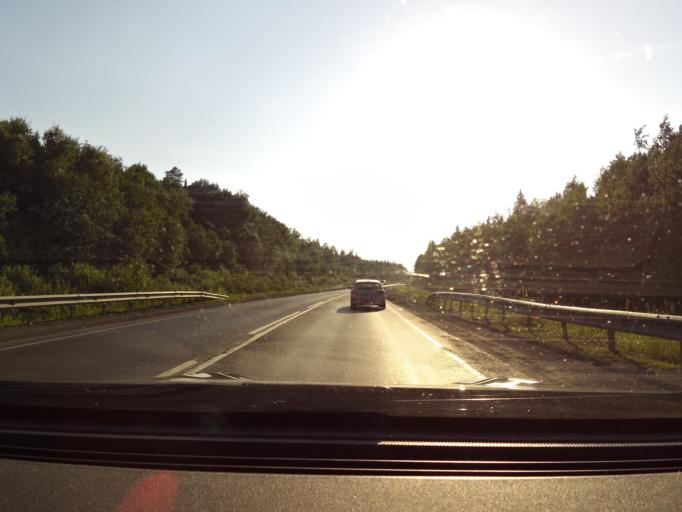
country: RU
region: Sverdlovsk
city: Bilimbay
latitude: 56.8584
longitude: 59.7426
